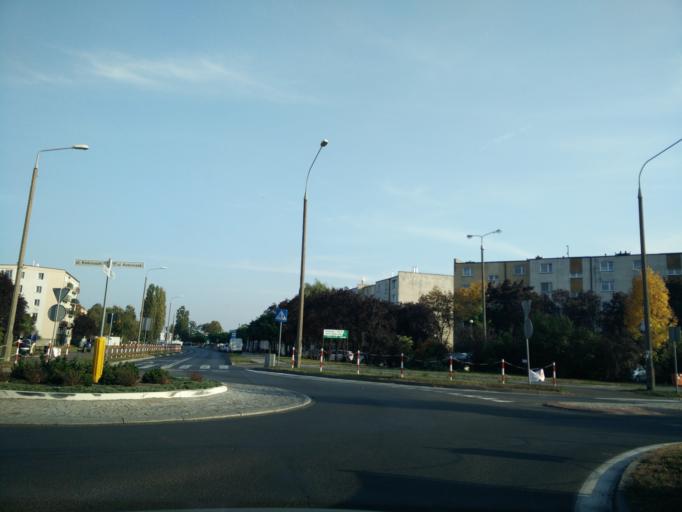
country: PL
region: Greater Poland Voivodeship
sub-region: Powiat sredzki
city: Sroda Wielkopolska
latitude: 52.2260
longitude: 17.2694
